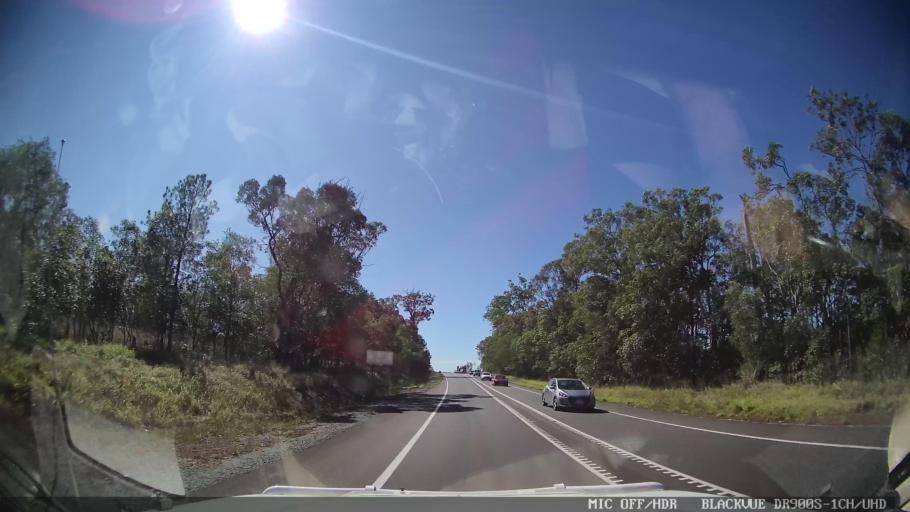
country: AU
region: Queensland
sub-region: Fraser Coast
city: Maryborough
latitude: -25.6491
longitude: 152.6346
